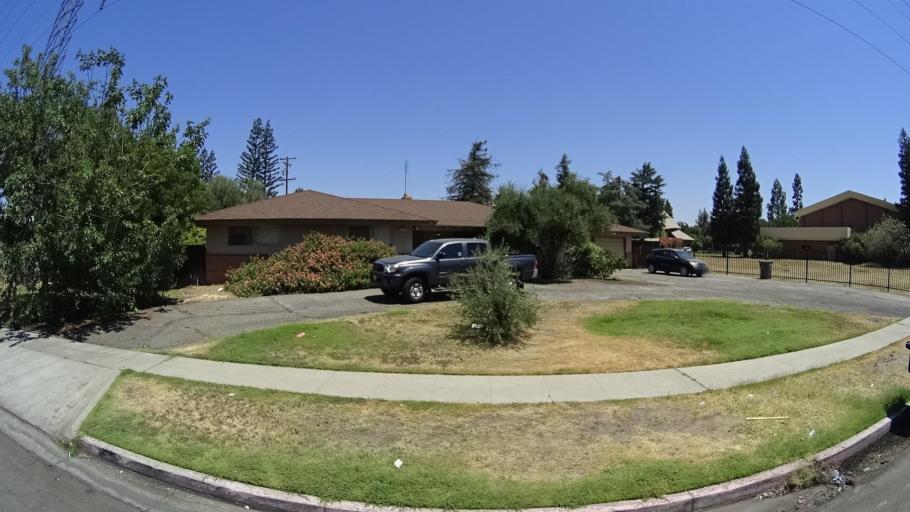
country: US
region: California
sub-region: Fresno County
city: Fresno
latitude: 36.7832
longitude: -119.7744
